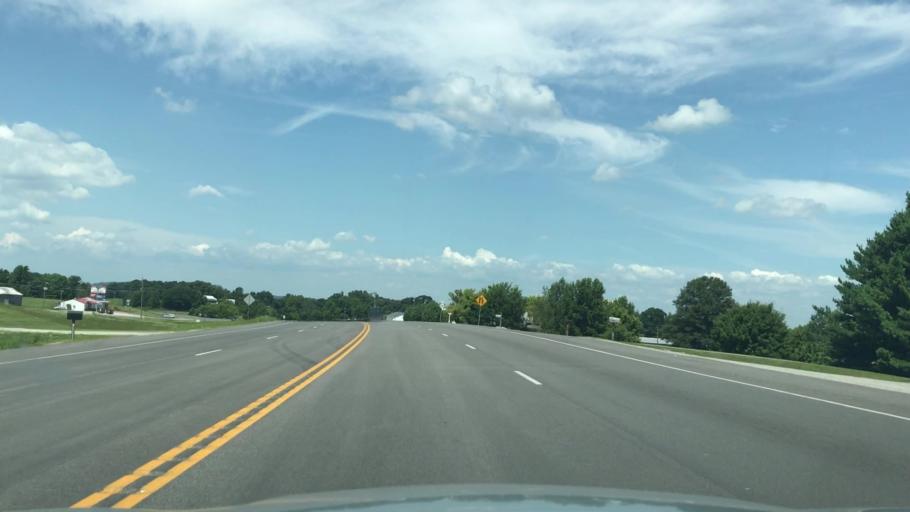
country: US
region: Kentucky
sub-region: Clinton County
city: Albany
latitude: 36.7537
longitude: -85.0933
